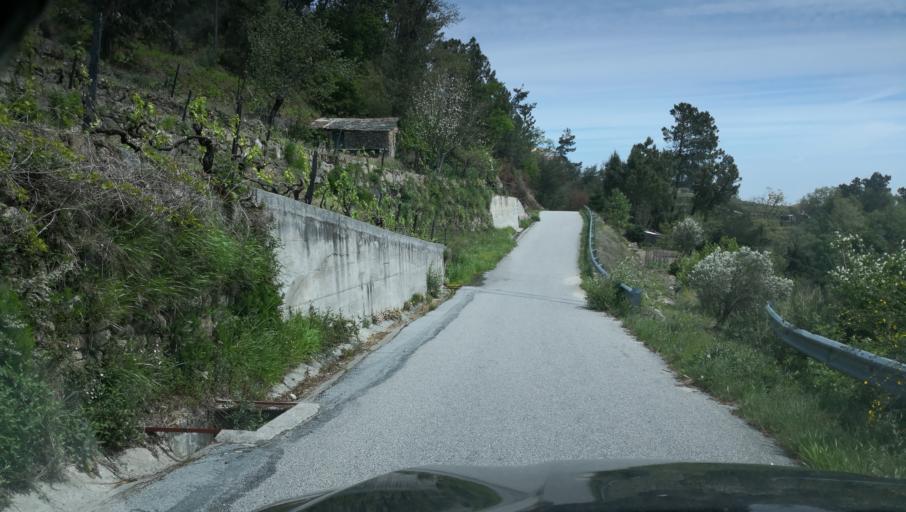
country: PT
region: Vila Real
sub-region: Vila Real
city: Vila Real
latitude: 41.3202
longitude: -7.7932
